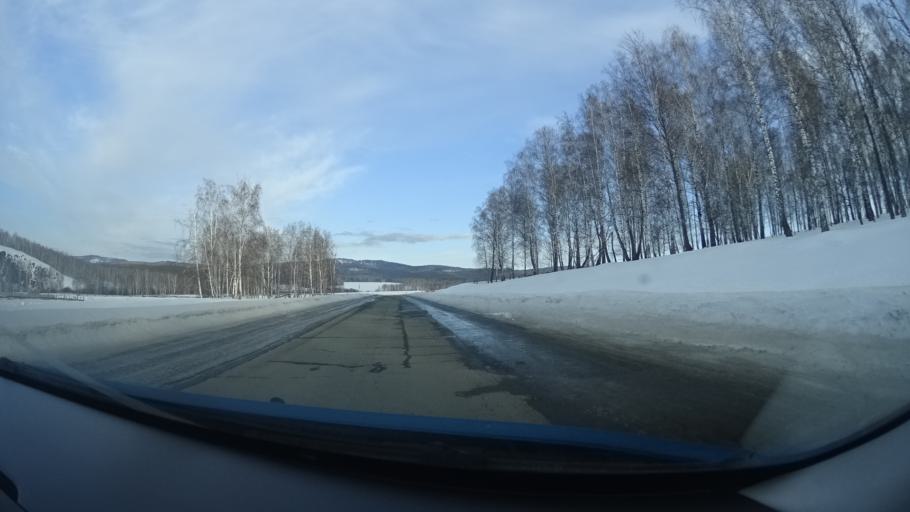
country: RU
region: Bashkortostan
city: Lomovka
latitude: 53.7217
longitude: 58.2466
